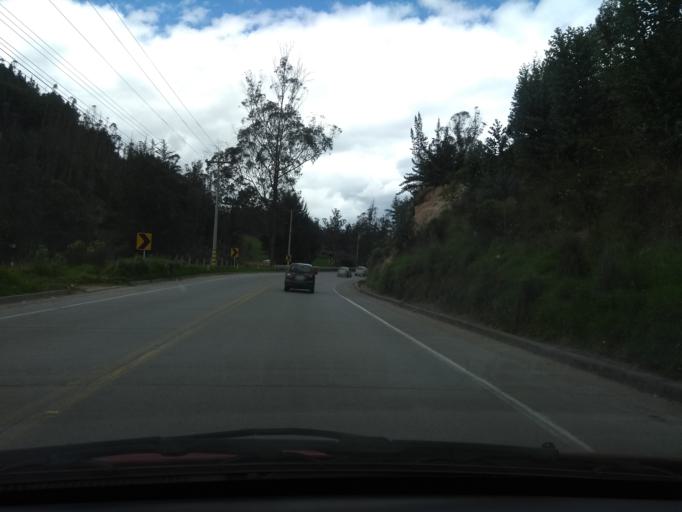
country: EC
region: Azuay
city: Cuenca
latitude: -3.0009
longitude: -79.0429
